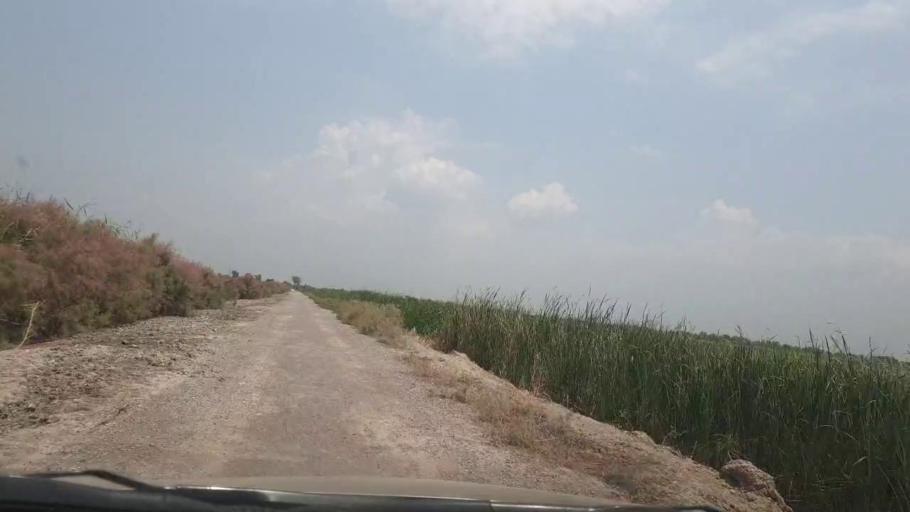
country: PK
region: Sindh
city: Naudero
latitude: 27.7224
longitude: 68.3231
